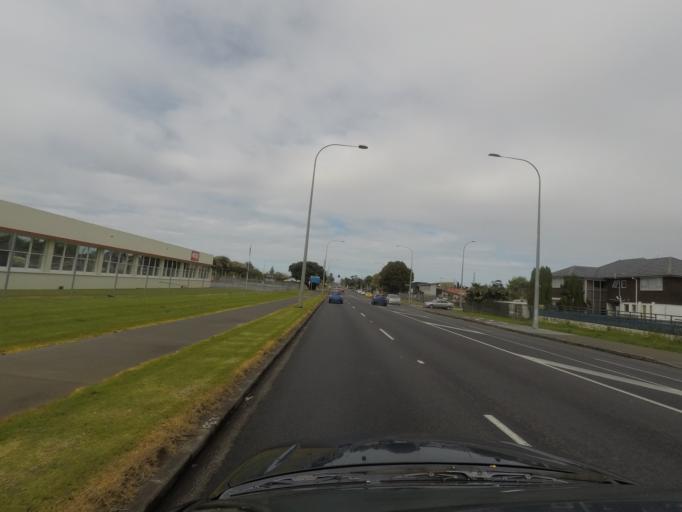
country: NZ
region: Auckland
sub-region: Auckland
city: Tamaki
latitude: -36.9016
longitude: 174.8430
